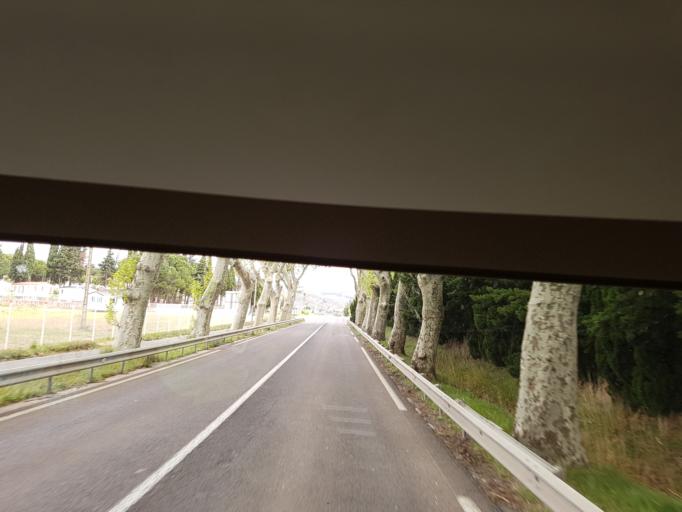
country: FR
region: Languedoc-Roussillon
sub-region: Departement des Pyrenees-Orientales
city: Salses-le-Chateau
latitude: 42.8420
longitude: 2.9260
